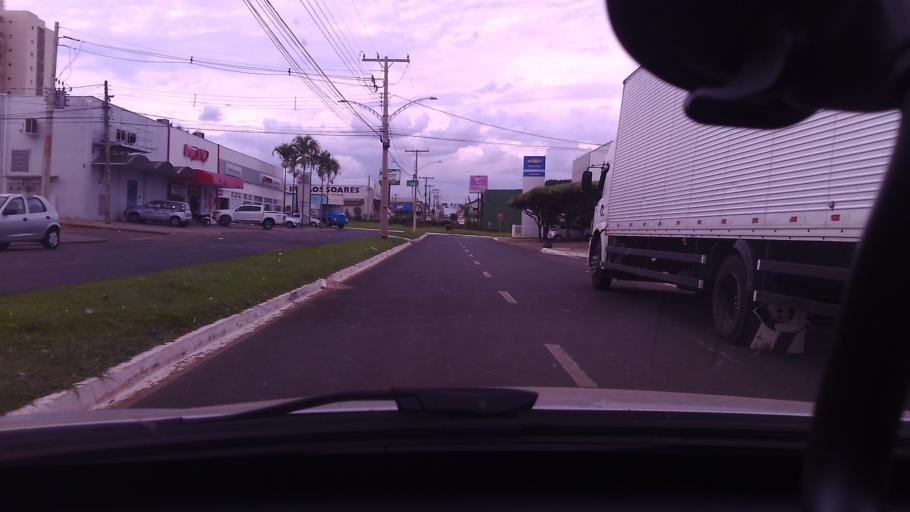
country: BR
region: Goias
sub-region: Mineiros
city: Mineiros
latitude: -17.5667
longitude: -52.5649
